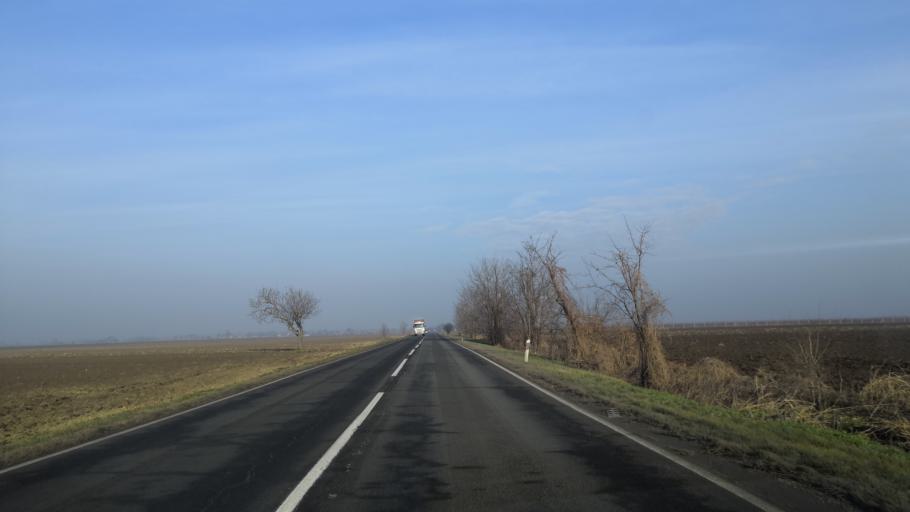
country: RS
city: Kisac
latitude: 45.3270
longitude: 19.7364
